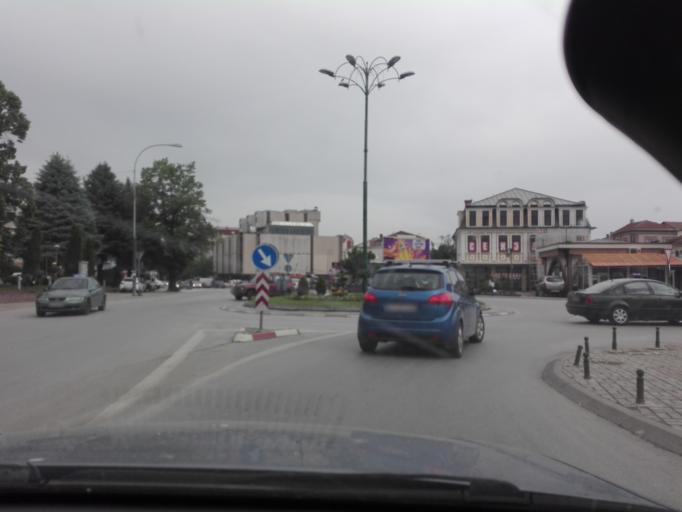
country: MK
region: Bitola
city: Bitola
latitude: 41.0322
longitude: 21.3352
